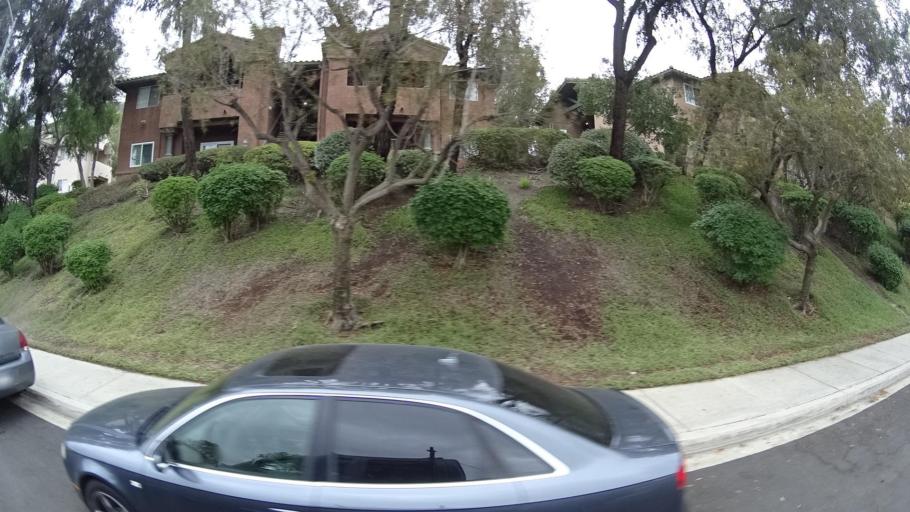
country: US
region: California
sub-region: San Diego County
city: Fairbanks Ranch
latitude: 33.0254
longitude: -117.1051
